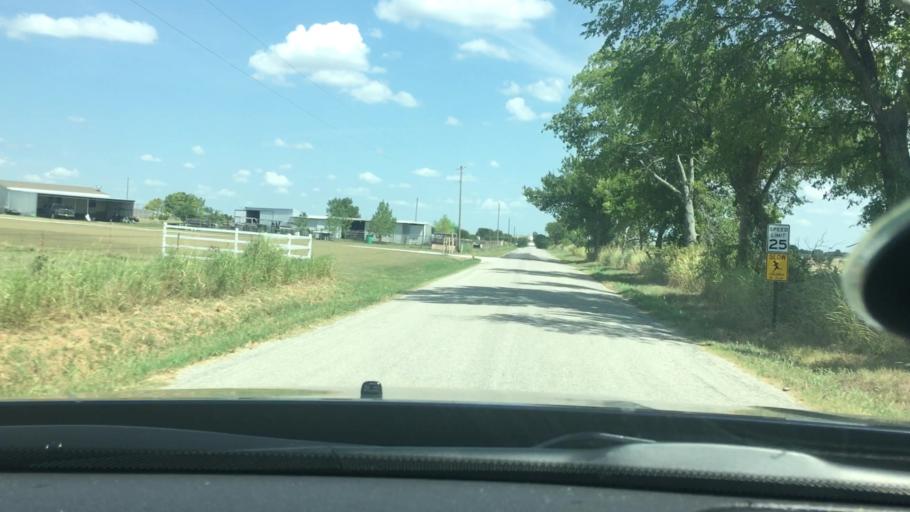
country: US
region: Oklahoma
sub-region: Love County
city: Marietta
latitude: 33.9416
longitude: -97.1869
